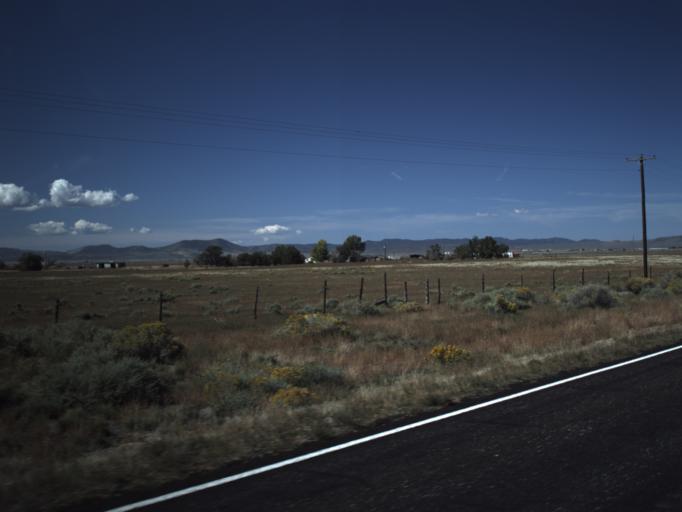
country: US
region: Utah
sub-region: Washington County
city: Enterprise
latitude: 37.6829
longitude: -113.5824
